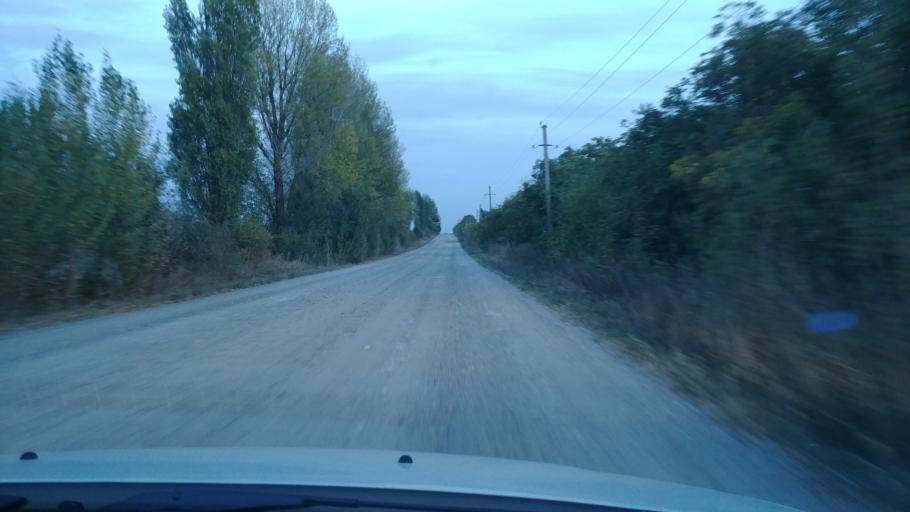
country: MD
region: Rezina
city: Saharna
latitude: 47.6722
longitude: 28.9386
